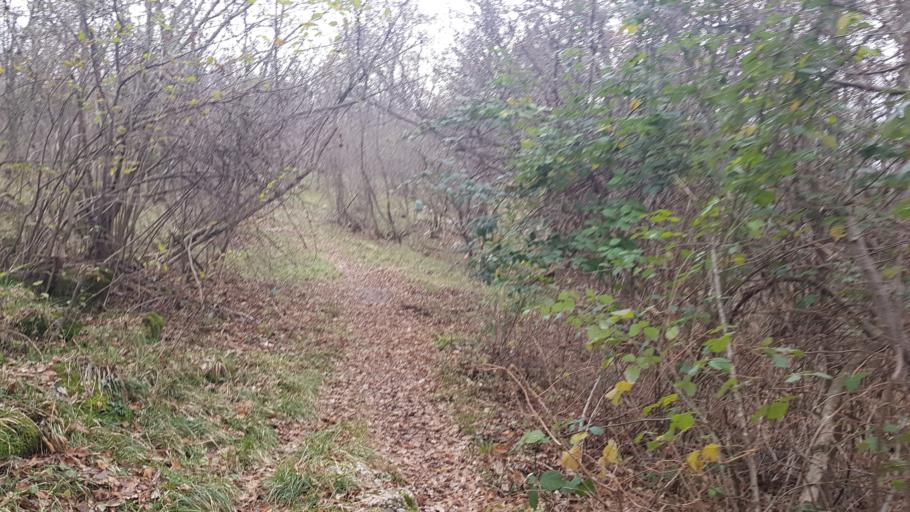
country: IT
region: Friuli Venezia Giulia
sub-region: Provincia di Trieste
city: Zolla
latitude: 45.7434
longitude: 13.7918
